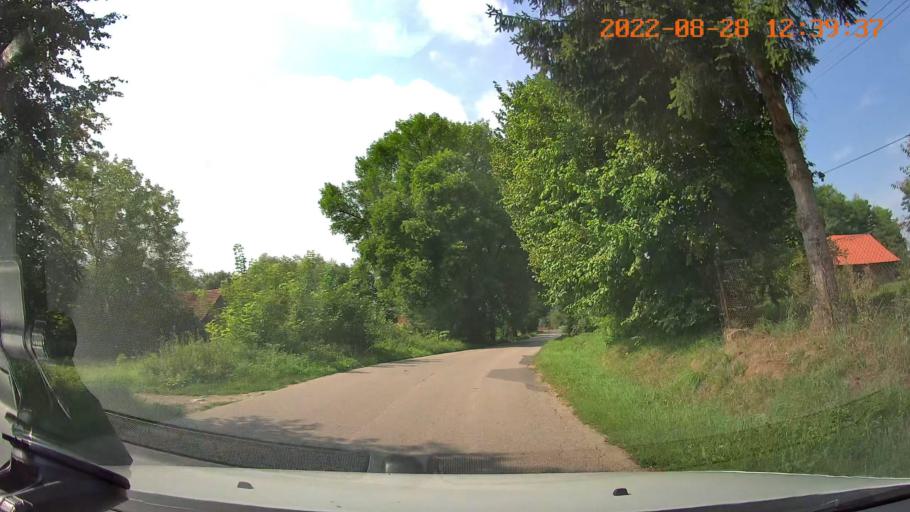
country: PL
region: Swietokrzyskie
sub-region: Powiat pinczowski
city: Dzialoszyce
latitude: 50.3727
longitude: 20.3720
